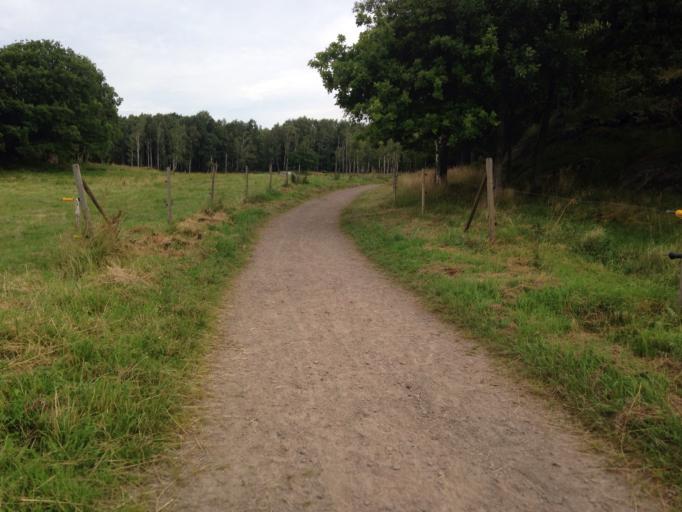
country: SE
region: Vaestra Goetaland
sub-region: Kungalvs Kommun
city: Kungalv
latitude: 57.8119
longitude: 11.8855
